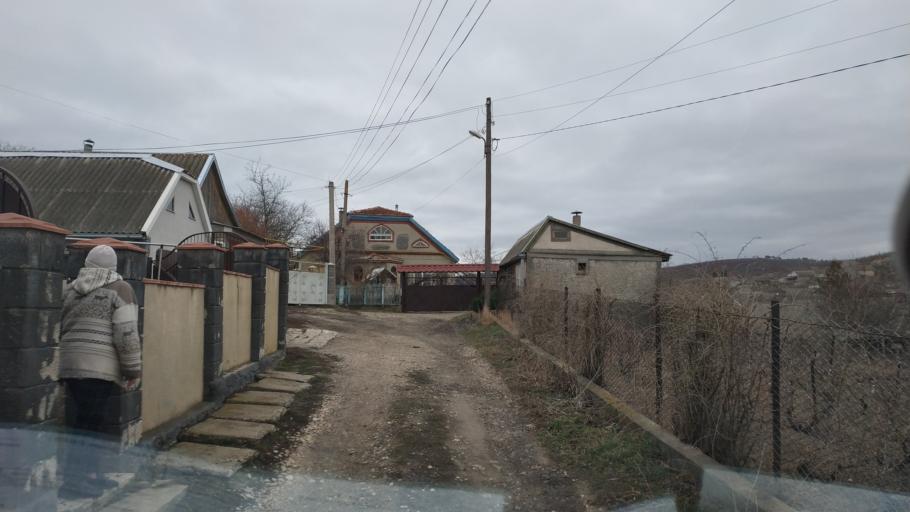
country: MD
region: Causeni
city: Causeni
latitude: 46.6480
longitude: 29.4410
